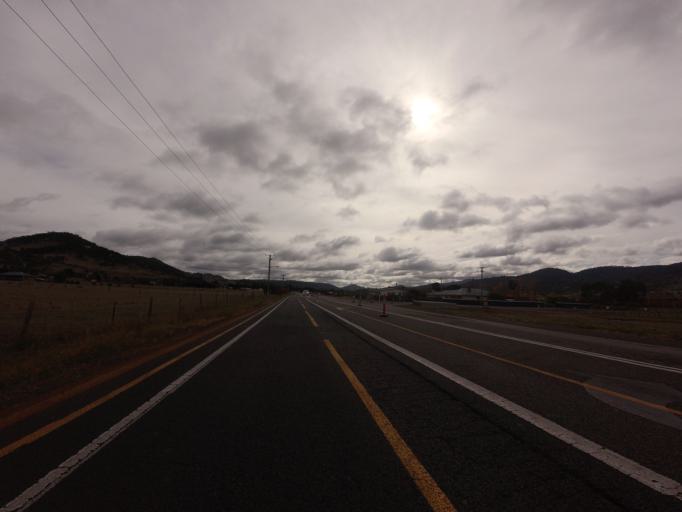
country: AU
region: Tasmania
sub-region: Brighton
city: Bridgewater
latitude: -42.6583
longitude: 147.2448
